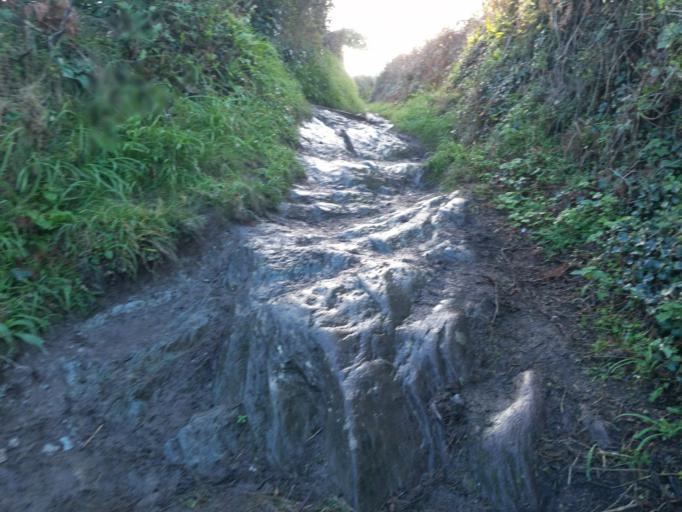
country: GB
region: England
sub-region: Cornwall
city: Looe
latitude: 50.3330
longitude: -4.5000
